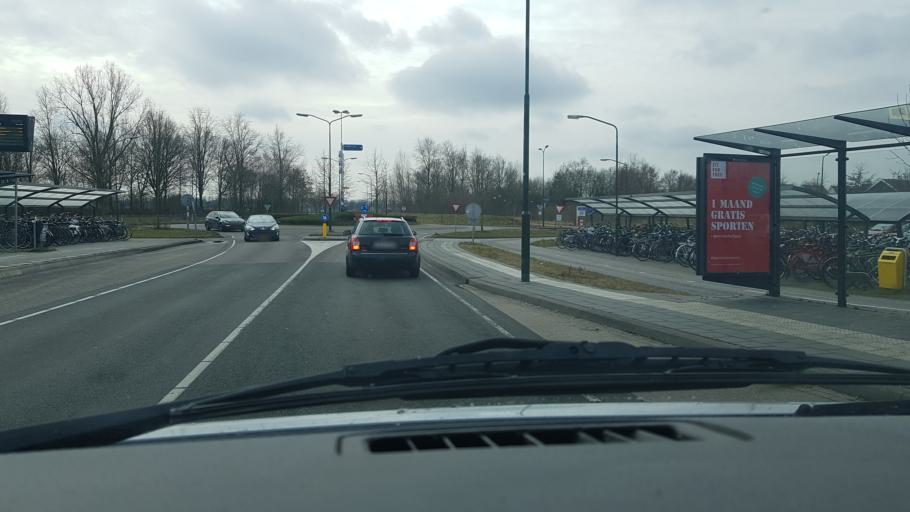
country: NL
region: North Brabant
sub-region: Gemeente Veghel
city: Mariaheide
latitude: 51.6346
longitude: 5.5679
